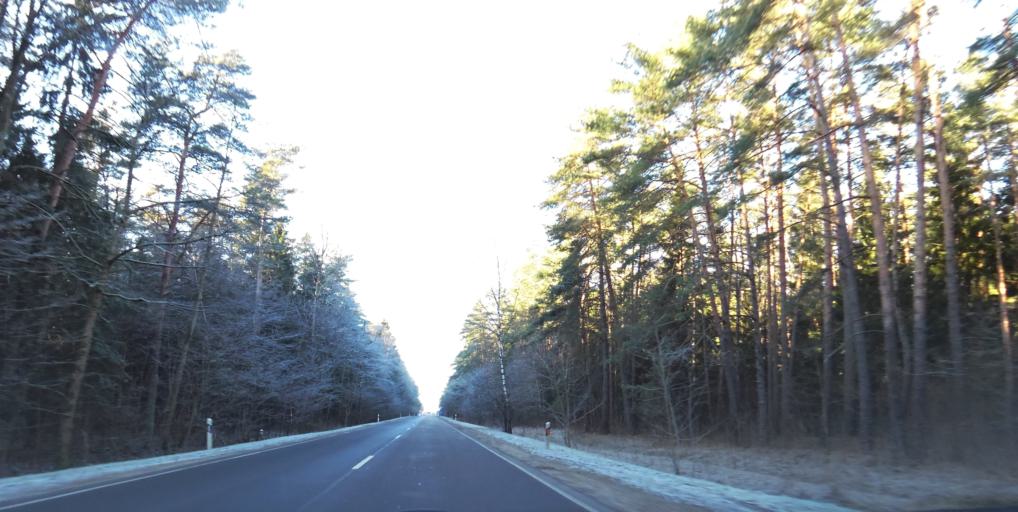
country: LT
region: Vilnius County
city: Lazdynai
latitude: 54.6435
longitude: 25.1618
